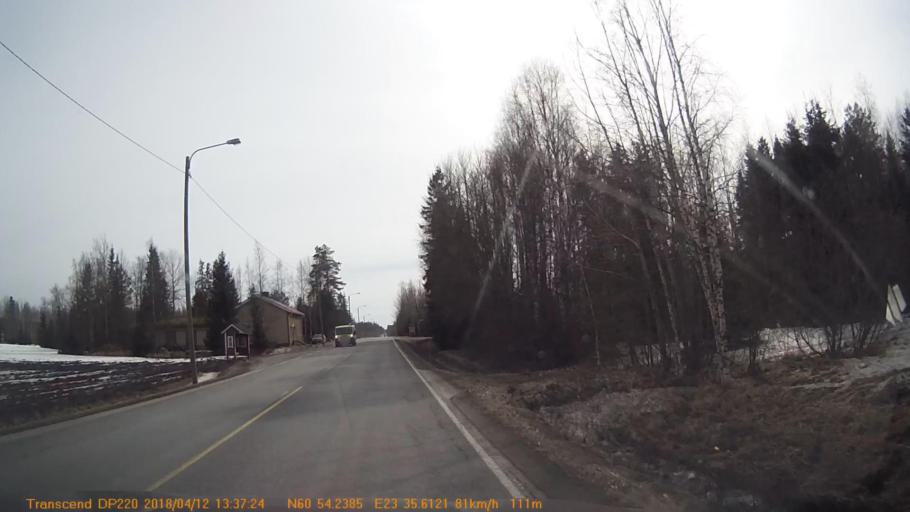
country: FI
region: Haeme
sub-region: Forssa
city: Forssa
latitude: 60.9036
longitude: 23.5937
